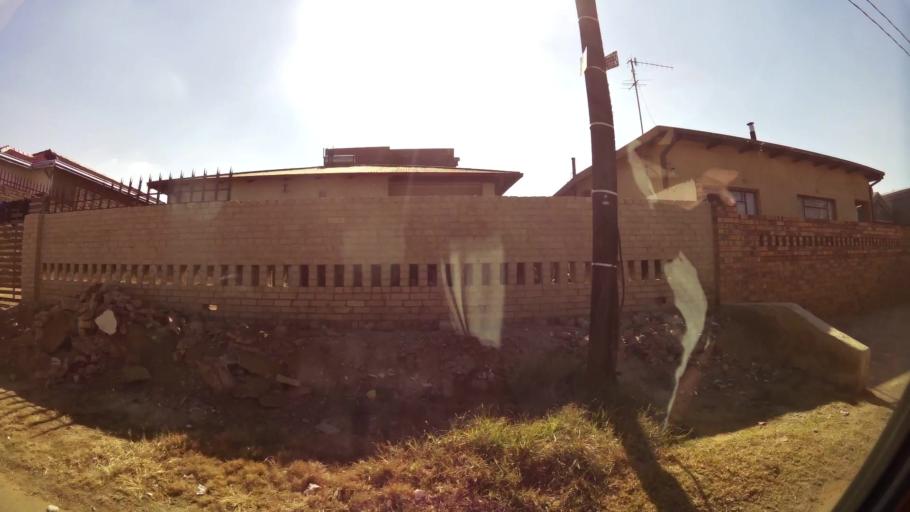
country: ZA
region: Gauteng
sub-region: City of Johannesburg Metropolitan Municipality
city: Soweto
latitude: -26.2449
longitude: 27.8973
